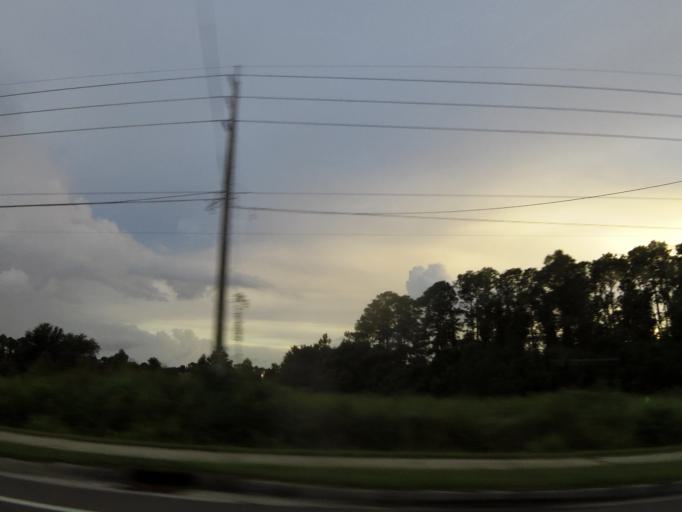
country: US
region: Florida
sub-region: Duval County
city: Jacksonville
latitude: 30.3551
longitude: -81.5457
